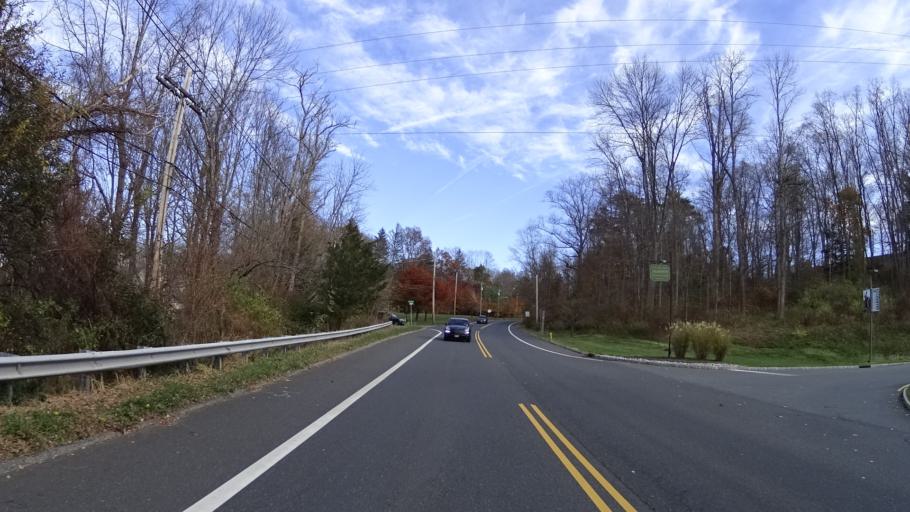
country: US
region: New Jersey
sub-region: Morris County
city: Morristown
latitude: 40.7921
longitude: -74.5299
